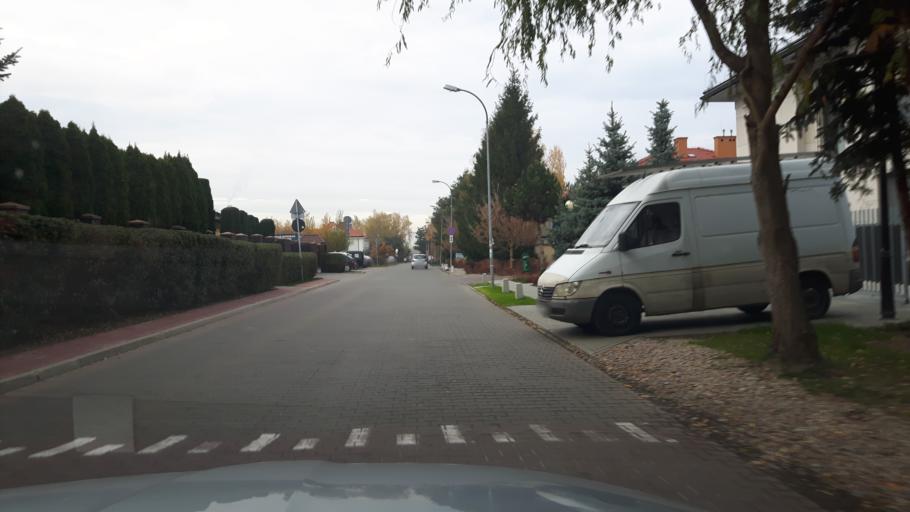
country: PL
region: Masovian Voivodeship
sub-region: Warszawa
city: Wilanow
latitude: 52.1700
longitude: 21.1149
